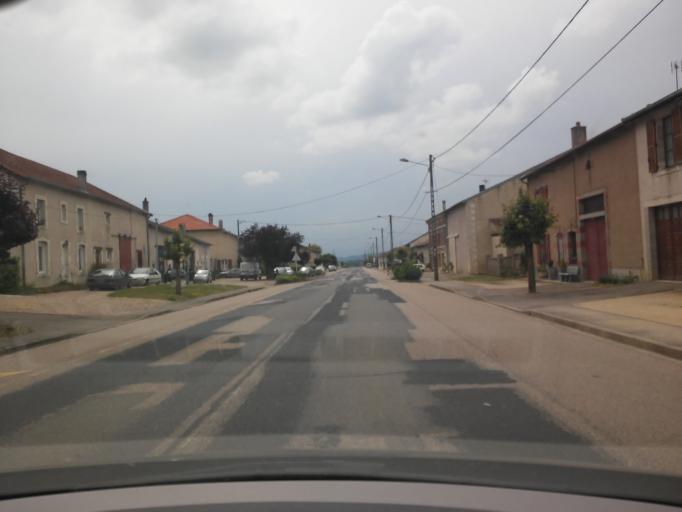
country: FR
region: Lorraine
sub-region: Departement de la Meuse
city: Vigneulles-les-Hattonchatel
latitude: 48.8436
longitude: 5.7570
